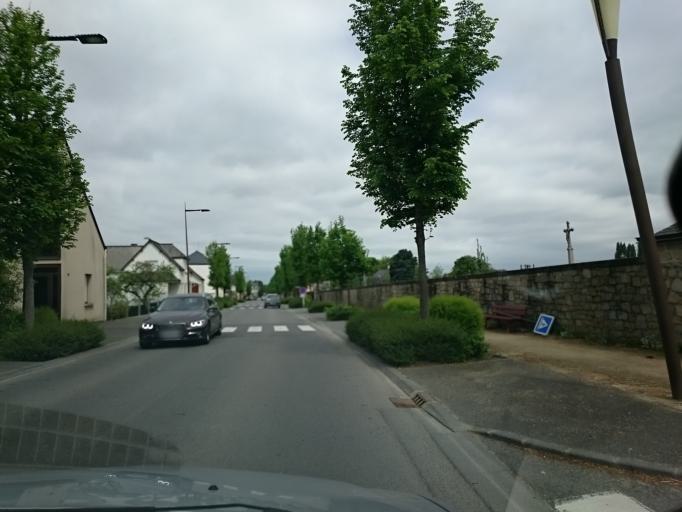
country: FR
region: Lower Normandy
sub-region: Departement de la Manche
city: Pontorson
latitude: 48.5545
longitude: -1.5065
